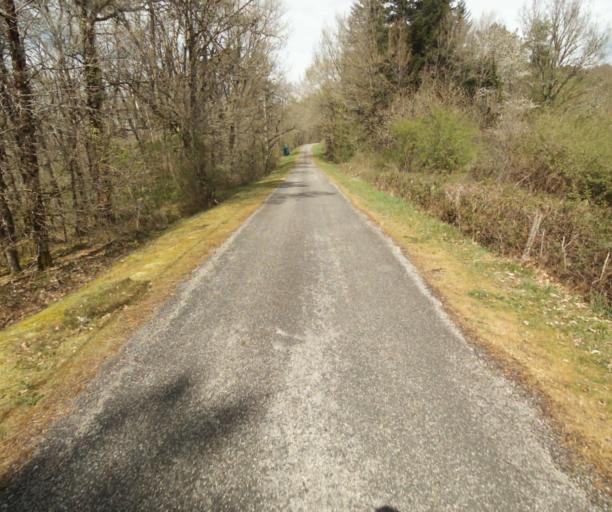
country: FR
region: Limousin
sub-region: Departement de la Correze
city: Sainte-Fortunade
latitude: 45.1784
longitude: 1.8710
